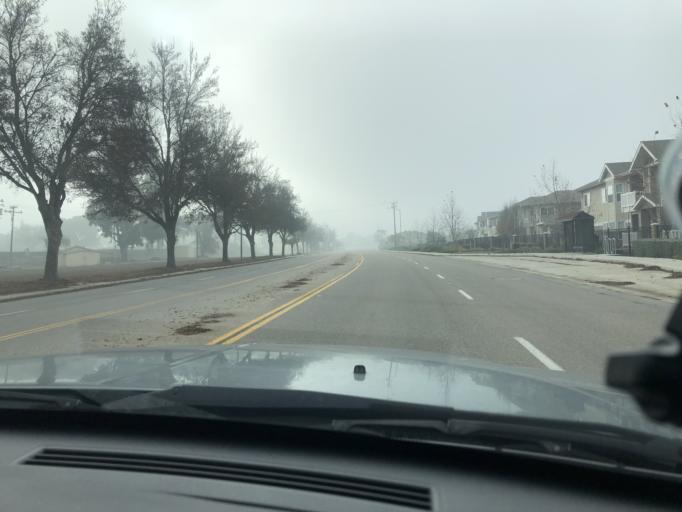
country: US
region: California
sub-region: Monterey County
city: King City
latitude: 36.2089
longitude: -121.1399
